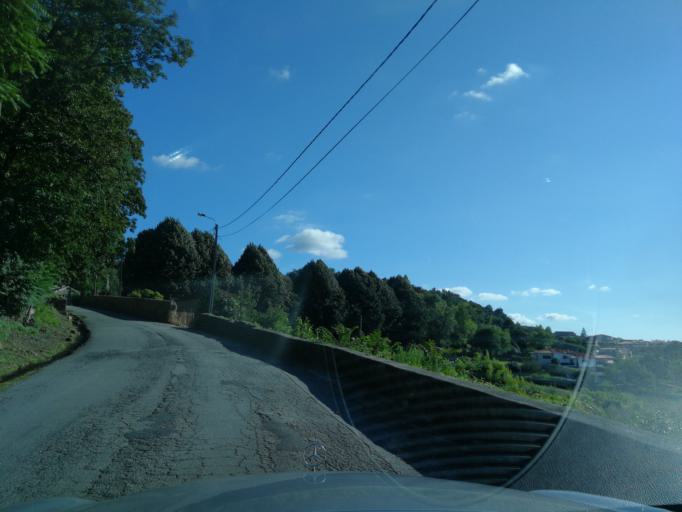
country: PT
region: Braga
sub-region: Braga
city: Adaufe
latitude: 41.5552
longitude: -8.3815
